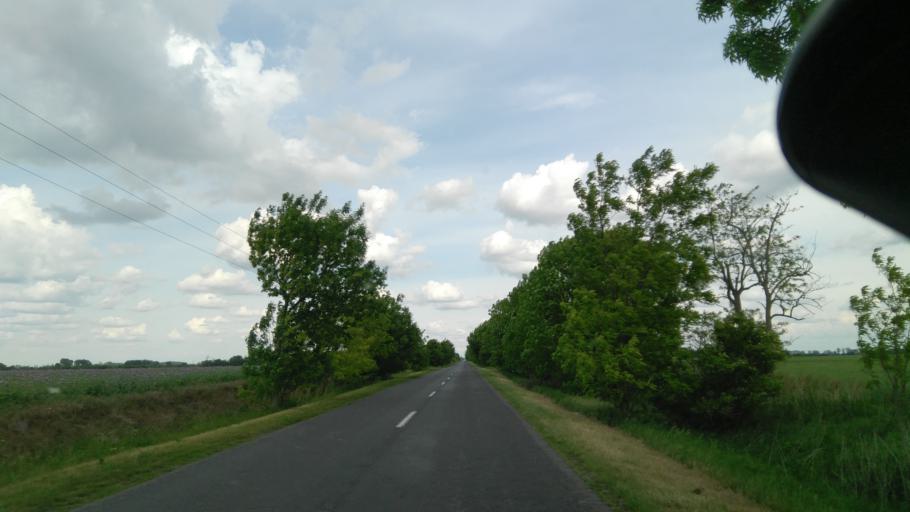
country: RO
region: Arad
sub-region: Comuna Peregu Mare
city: Peregu Mic
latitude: 46.2955
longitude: 20.9662
